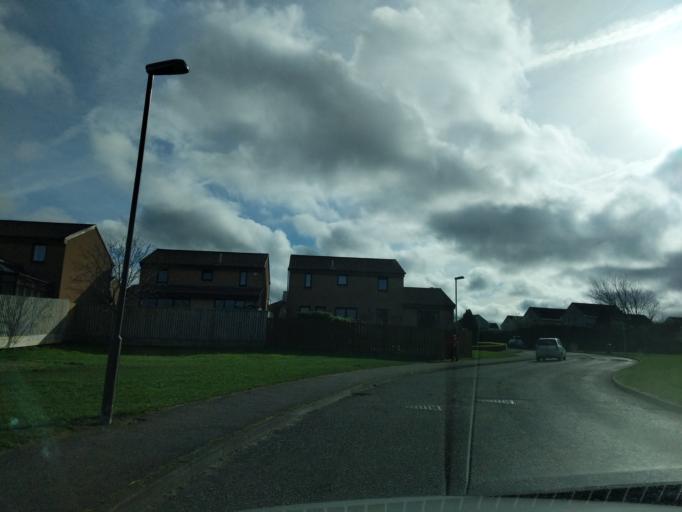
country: GB
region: Scotland
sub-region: Edinburgh
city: Queensferry
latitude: 55.9878
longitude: -3.4085
